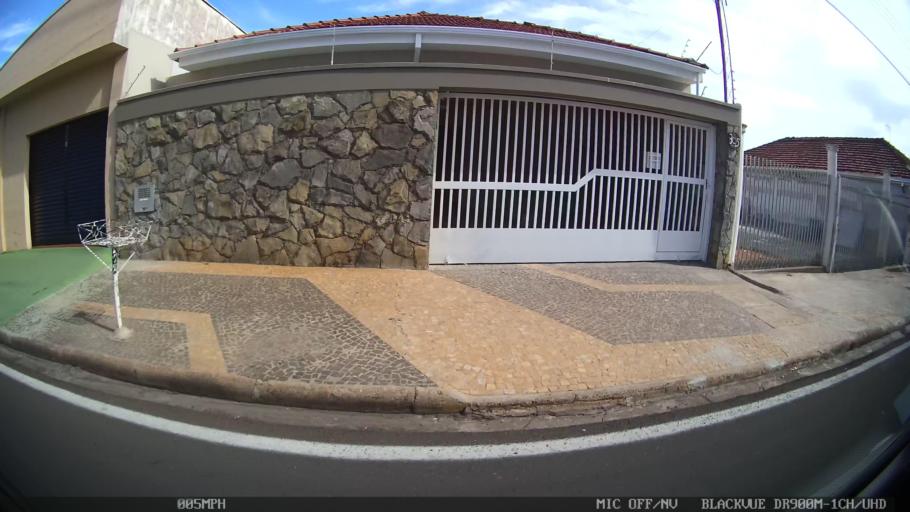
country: BR
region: Sao Paulo
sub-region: Catanduva
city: Catanduva
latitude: -21.1335
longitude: -48.9659
